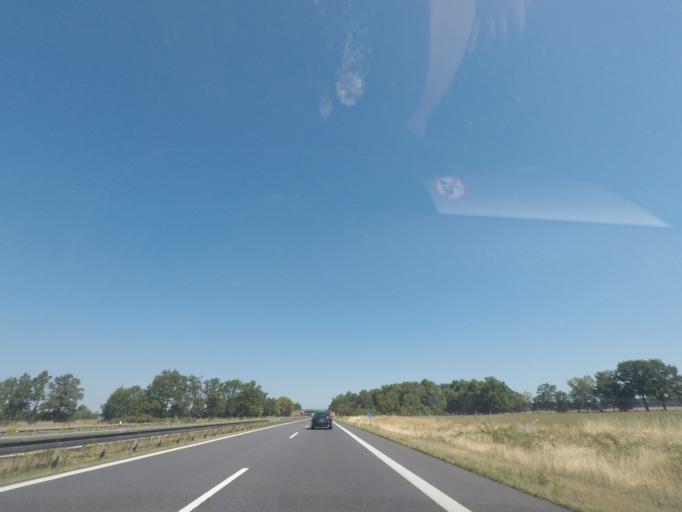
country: DE
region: Brandenburg
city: Calau
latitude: 51.7545
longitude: 13.8631
